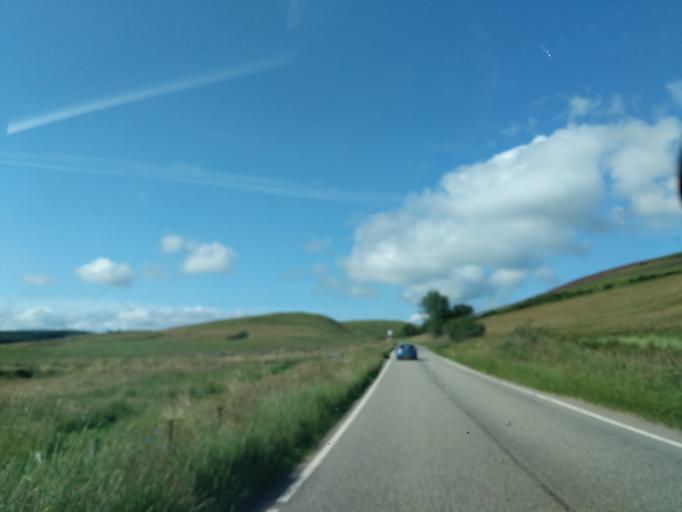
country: GB
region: Scotland
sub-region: Moray
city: Dufftown
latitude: 57.3742
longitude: -3.2319
